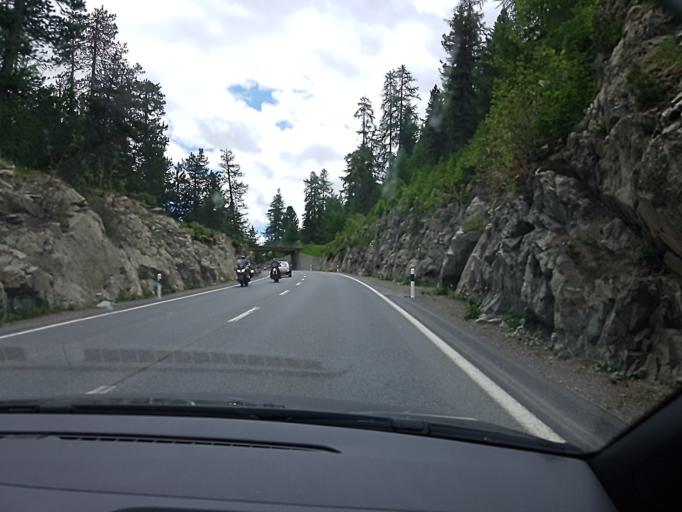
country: CH
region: Grisons
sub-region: Maloja District
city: Pontresina
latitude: 46.4884
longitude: 9.9041
